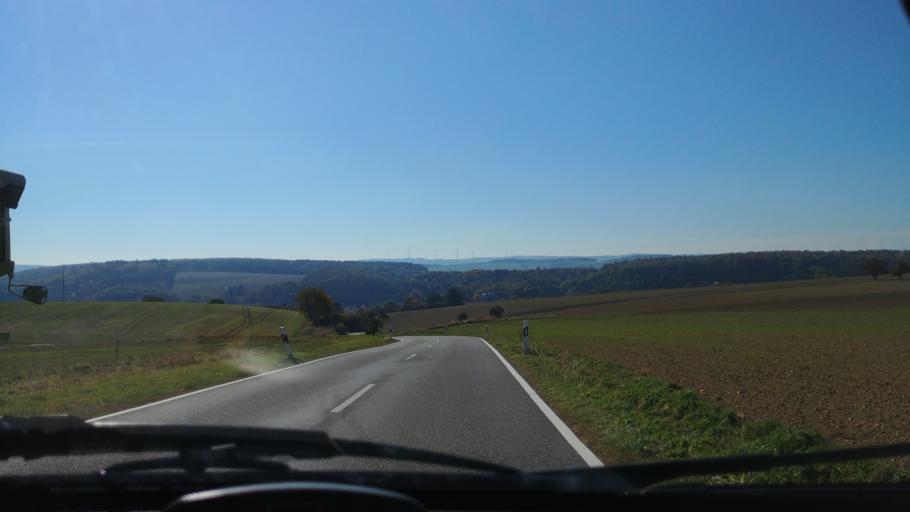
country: DE
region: Rheinland-Pfalz
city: Burgschwalbach
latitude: 50.2376
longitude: 8.1253
